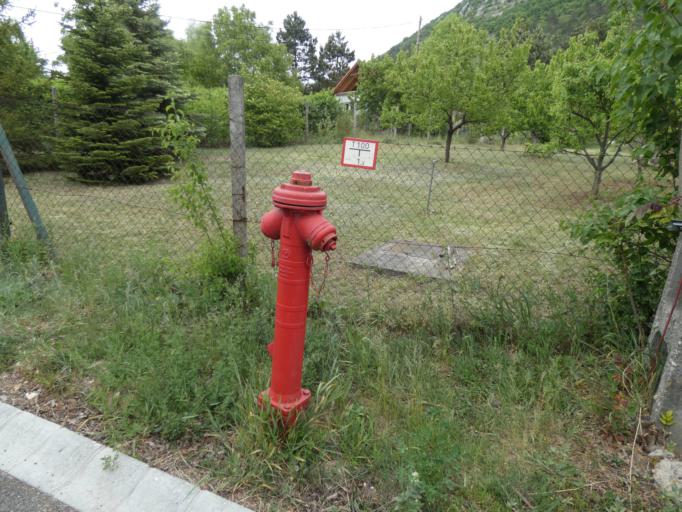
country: HU
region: Pest
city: Pilisborosjeno
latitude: 47.6166
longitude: 18.9864
